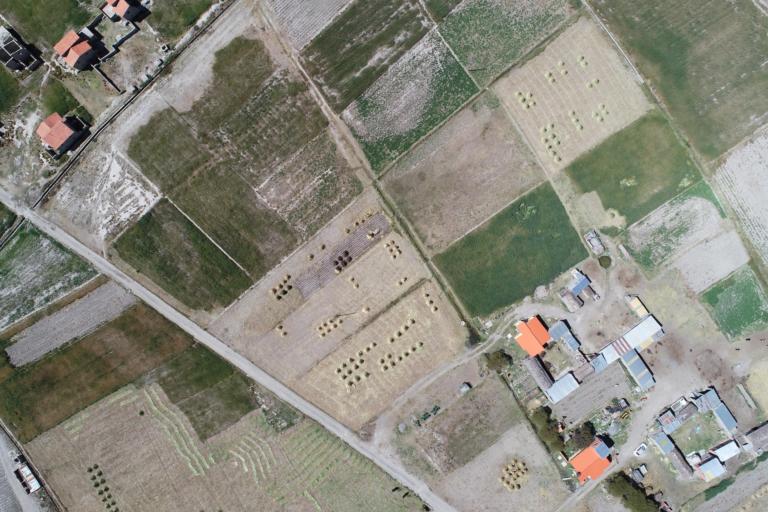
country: BO
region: La Paz
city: Achacachi
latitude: -16.0185
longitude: -68.7183
